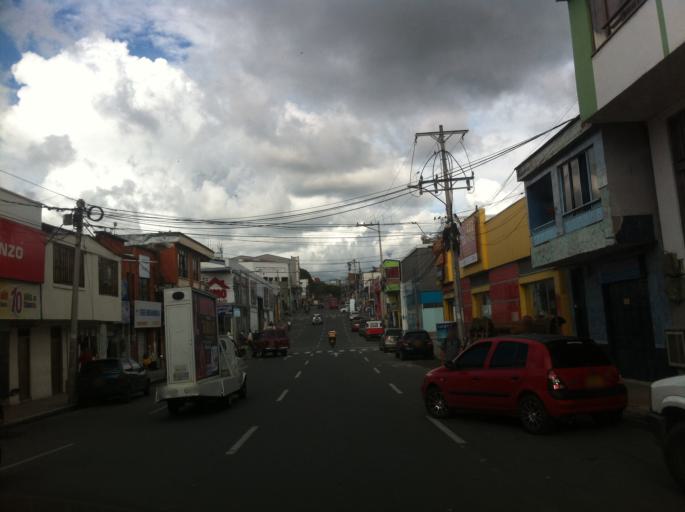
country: CO
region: Quindio
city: Armenia
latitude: 4.5387
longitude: -75.6706
